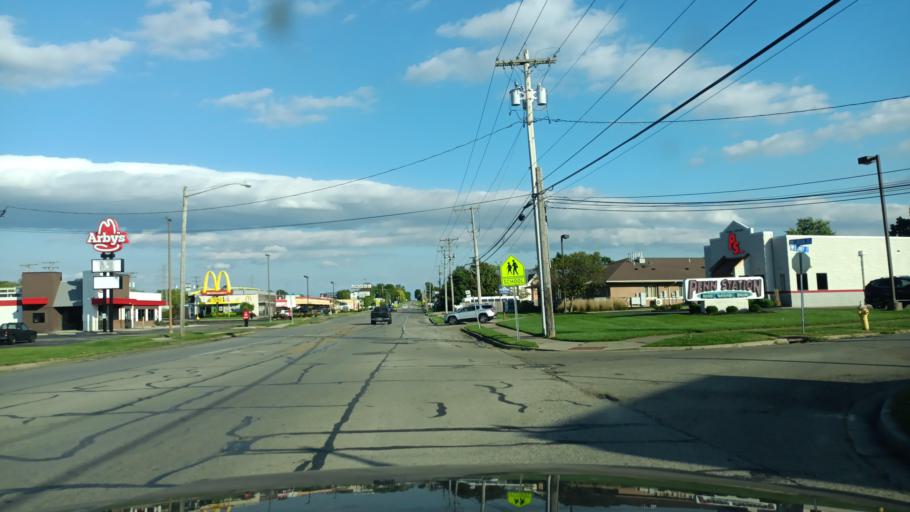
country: US
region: Ohio
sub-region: Montgomery County
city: Riverside
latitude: 39.7437
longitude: -84.1163
